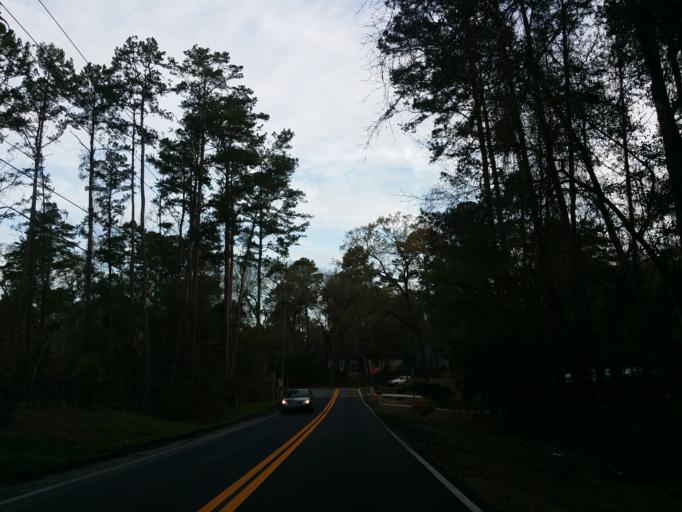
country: US
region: Florida
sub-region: Leon County
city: Tallahassee
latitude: 30.4754
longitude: -84.2189
